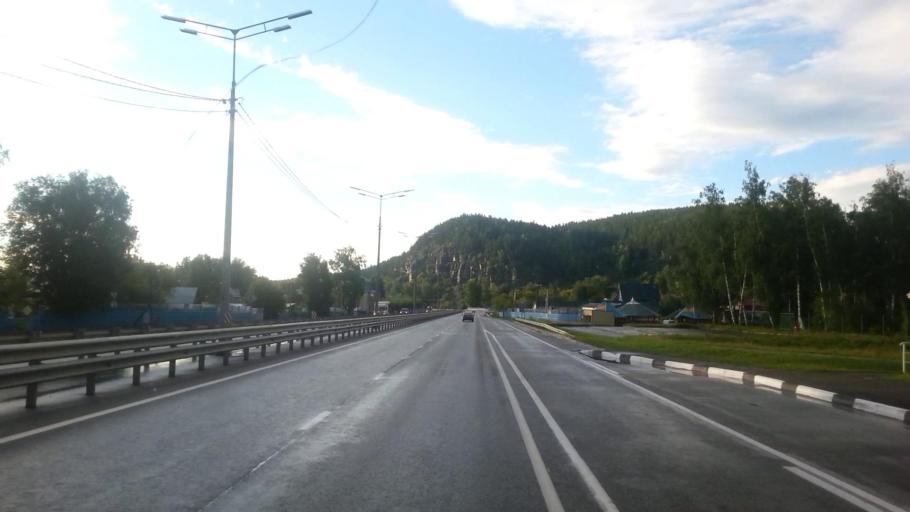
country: RU
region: Altay
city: Souzga
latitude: 51.9145
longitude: 85.8627
